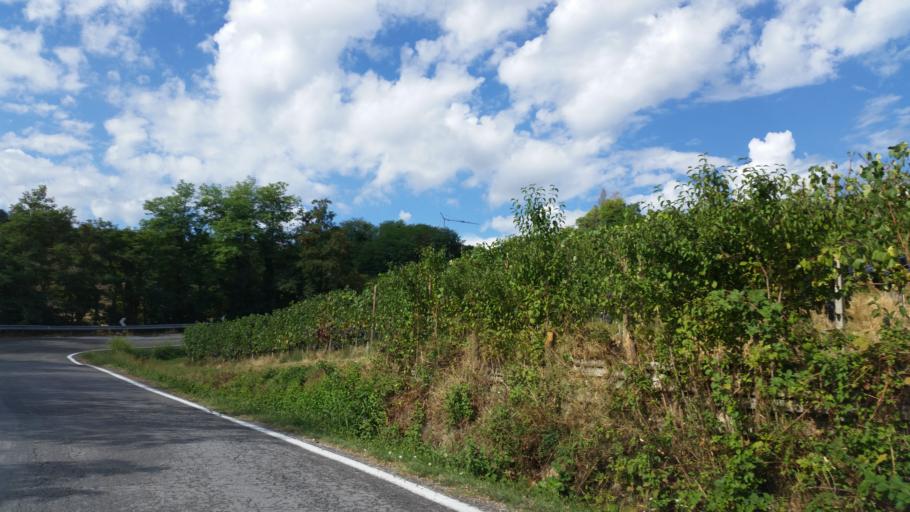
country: IT
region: Piedmont
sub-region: Provincia di Cuneo
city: Castagnito
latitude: 44.7569
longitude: 8.0401
